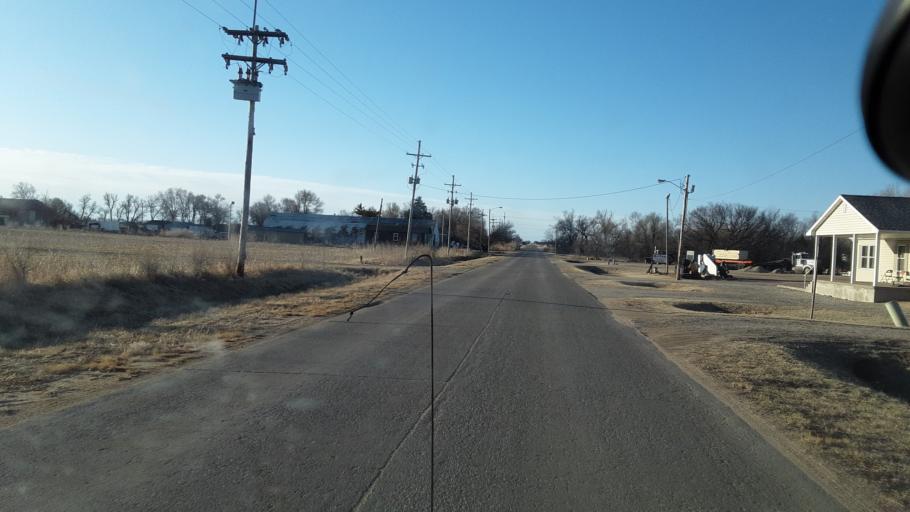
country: US
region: Kansas
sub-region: Rice County
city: Lyons
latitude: 38.3509
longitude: -98.3495
